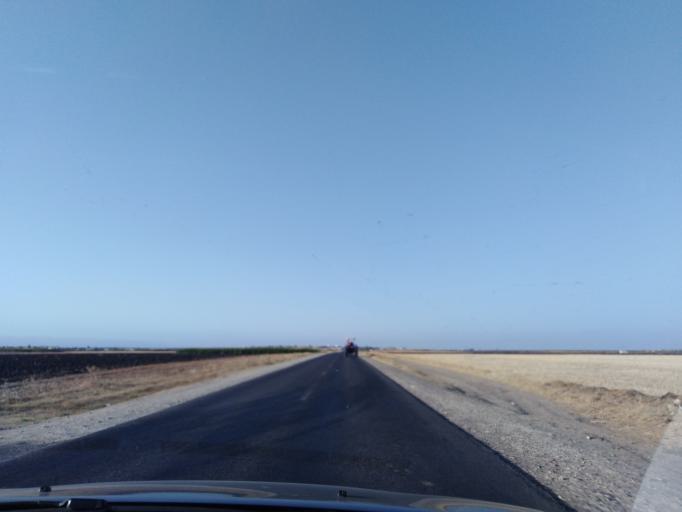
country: MA
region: Doukkala-Abda
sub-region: Safi
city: Safi
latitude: 32.5122
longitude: -8.9163
